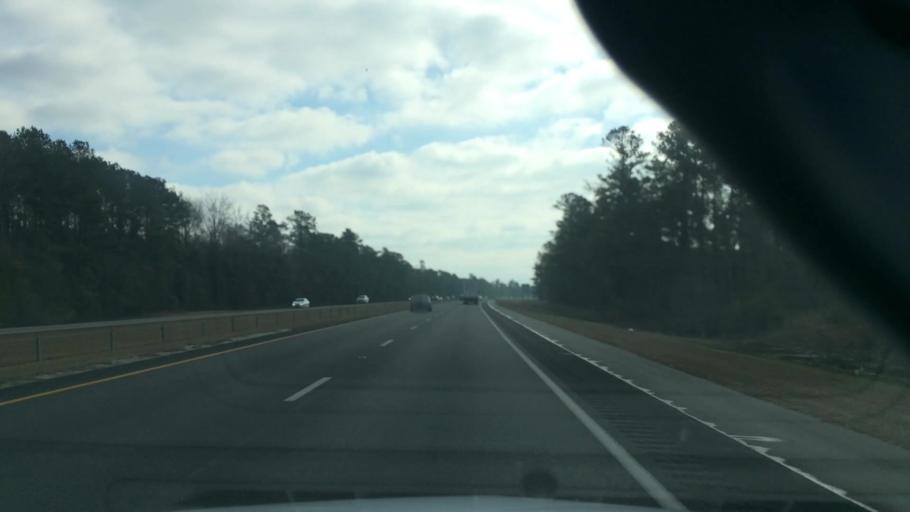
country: US
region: North Carolina
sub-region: Pender County
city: Burgaw
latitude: 34.5639
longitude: -77.8970
